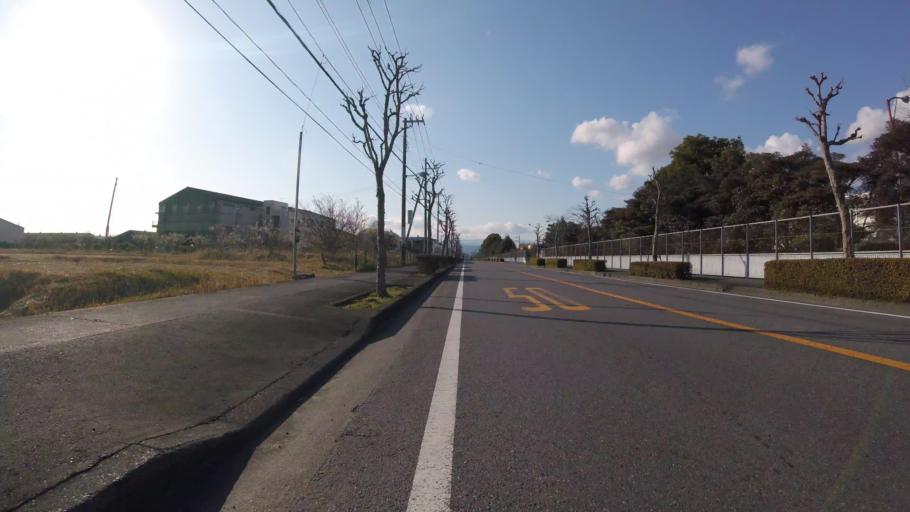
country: JP
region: Shizuoka
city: Fuji
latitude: 35.1589
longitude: 138.7221
